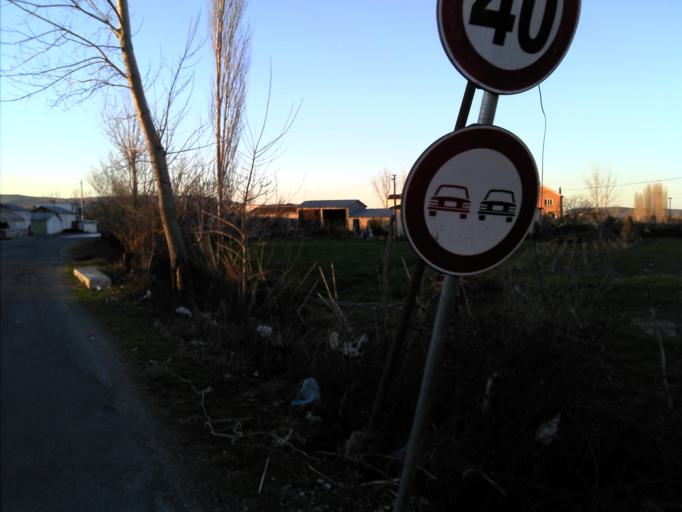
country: AL
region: Shkoder
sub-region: Rrethi i Shkodres
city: Berdica e Madhe
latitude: 41.9848
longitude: 19.4805
